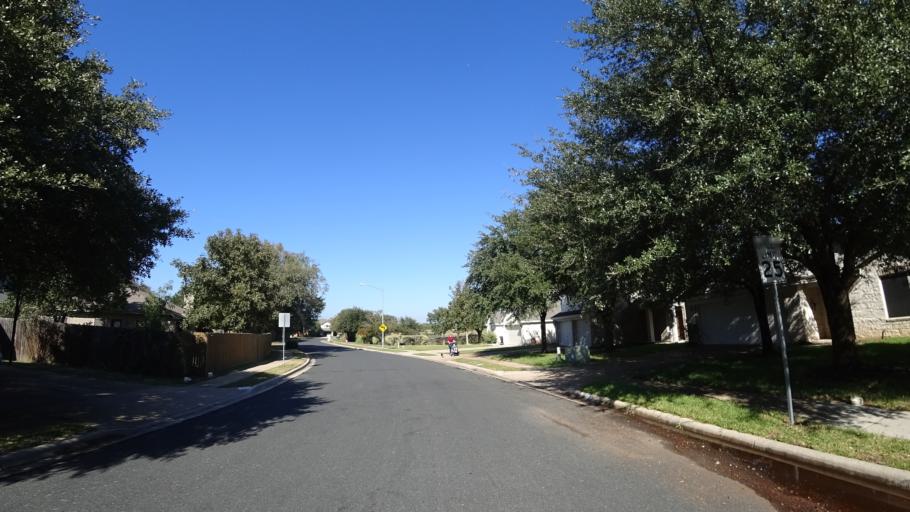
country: US
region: Texas
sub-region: Travis County
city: Shady Hollow
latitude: 30.1946
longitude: -97.8573
